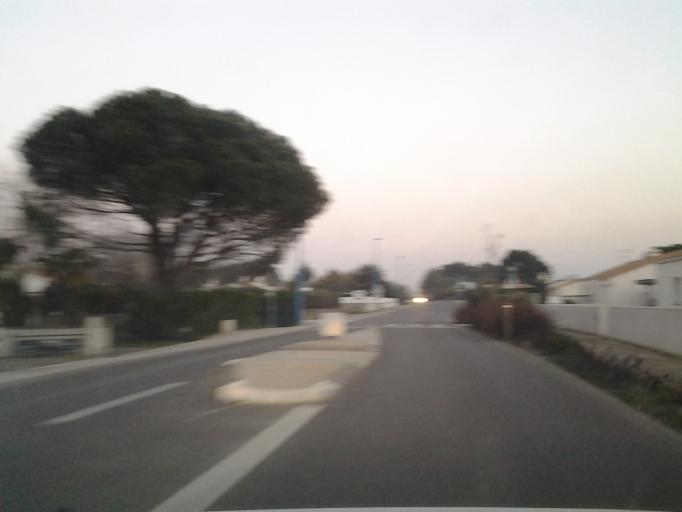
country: FR
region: Pays de la Loire
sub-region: Departement de la Vendee
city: Beauvoir-sur-Mer
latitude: 46.9074
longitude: -2.0275
